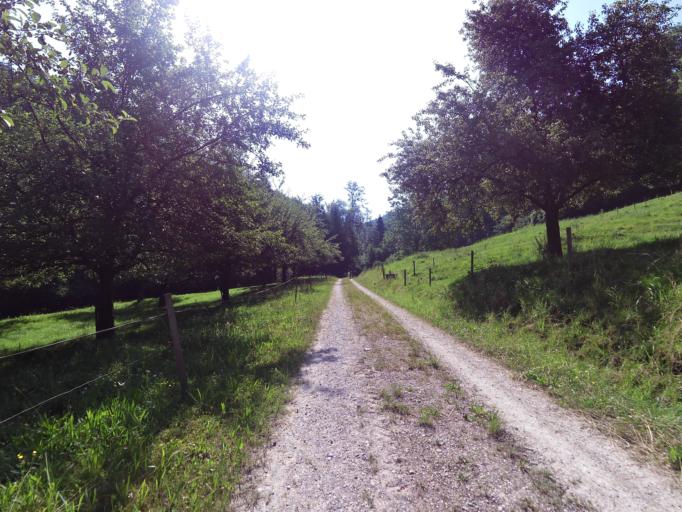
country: CH
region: Thurgau
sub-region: Frauenfeld District
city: Mullheim
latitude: 47.5761
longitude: 8.9827
